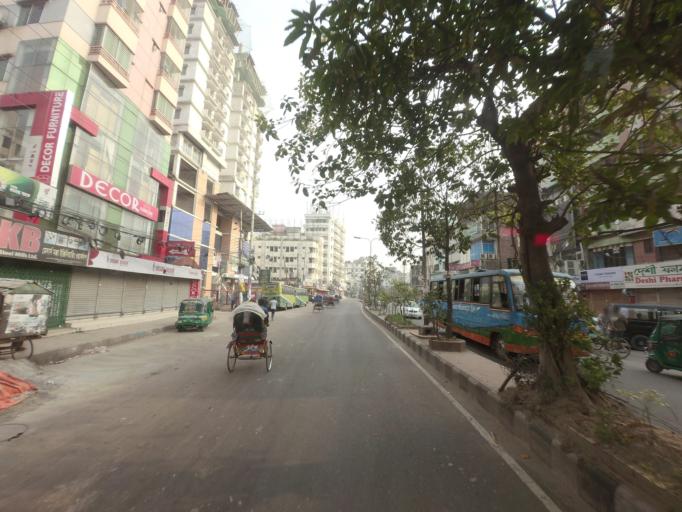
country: BD
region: Dhaka
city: Azimpur
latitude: 23.7689
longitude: 90.3585
